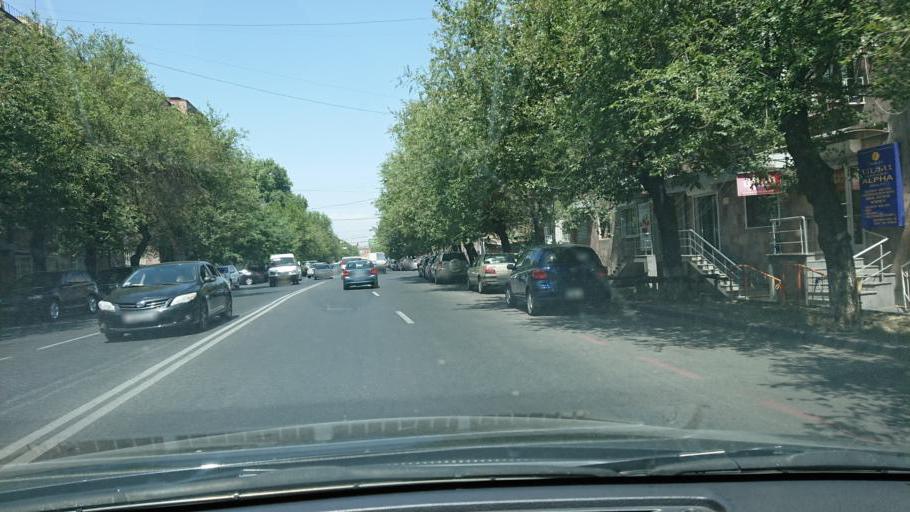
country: AM
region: Yerevan
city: Yerevan
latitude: 40.2013
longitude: 44.4997
